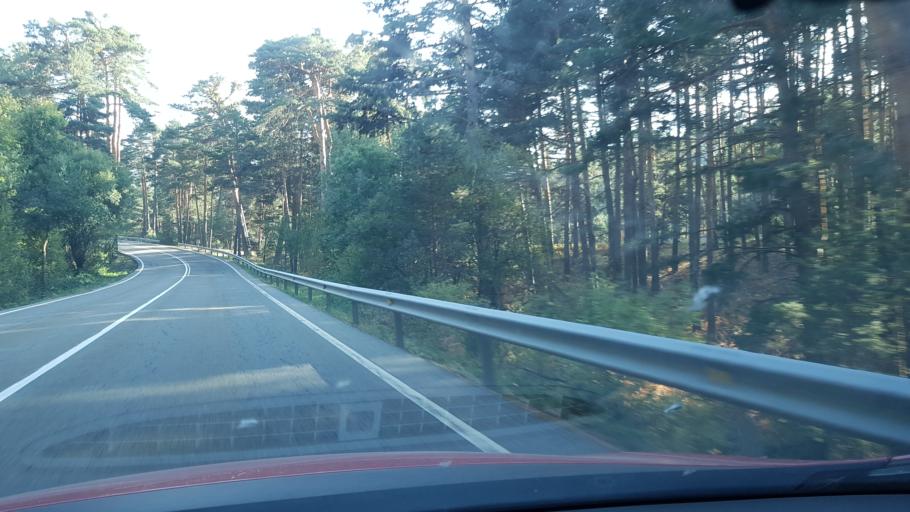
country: ES
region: Castille and Leon
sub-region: Provincia de Segovia
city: San Ildefonso
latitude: 40.8341
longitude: -4.0245
